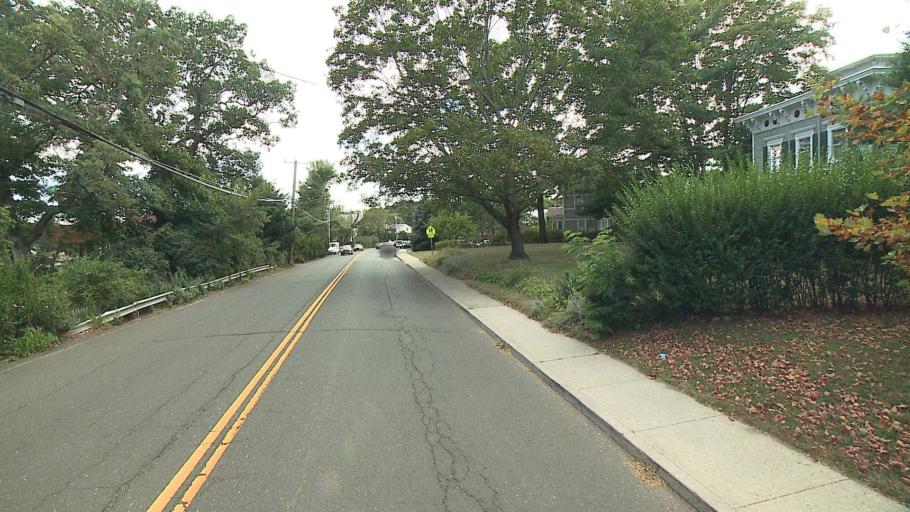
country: US
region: Connecticut
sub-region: Fairfield County
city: Westport
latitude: 41.1358
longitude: -73.3649
